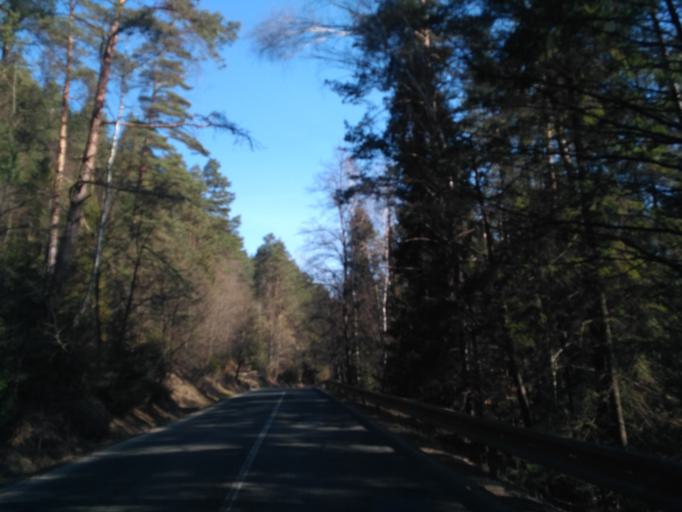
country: SK
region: Kosicky
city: Medzev
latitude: 48.7663
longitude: 20.7798
